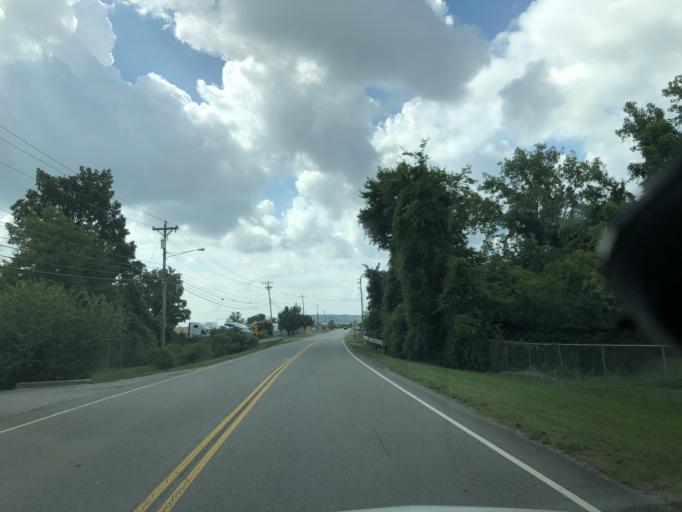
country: US
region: Tennessee
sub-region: Rutherford County
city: La Vergne
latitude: 36.0108
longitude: -86.6089
